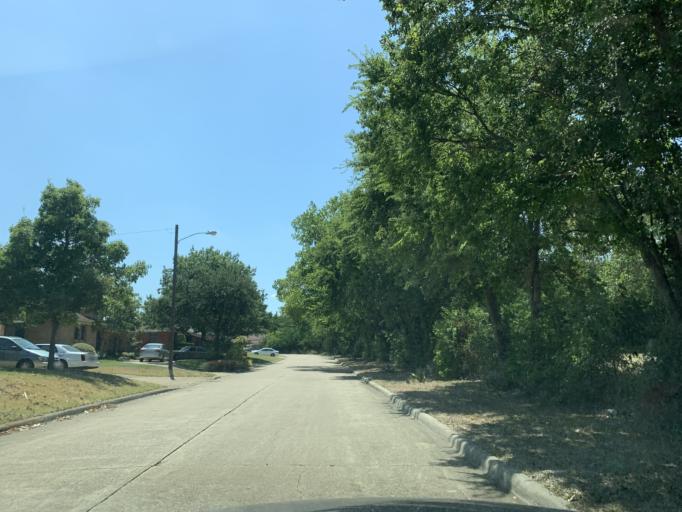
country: US
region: Texas
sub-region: Dallas County
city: Cockrell Hill
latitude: 32.6774
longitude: -96.8104
